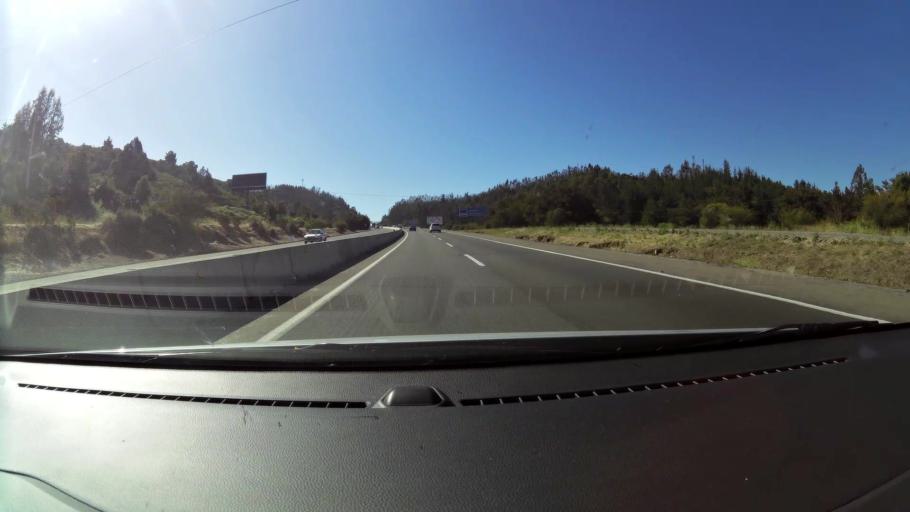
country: CL
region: Valparaiso
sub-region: Provincia de Marga Marga
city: Quilpue
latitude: -33.2140
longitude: -71.4751
